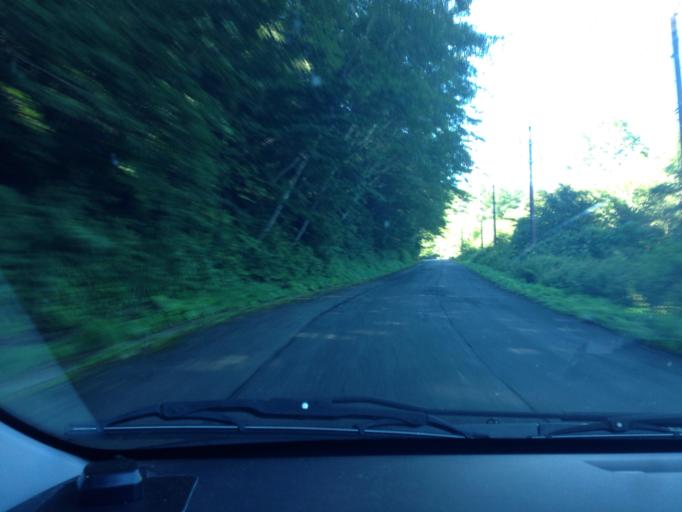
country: JP
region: Fukushima
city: Inawashiro
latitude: 37.3407
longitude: 140.0607
